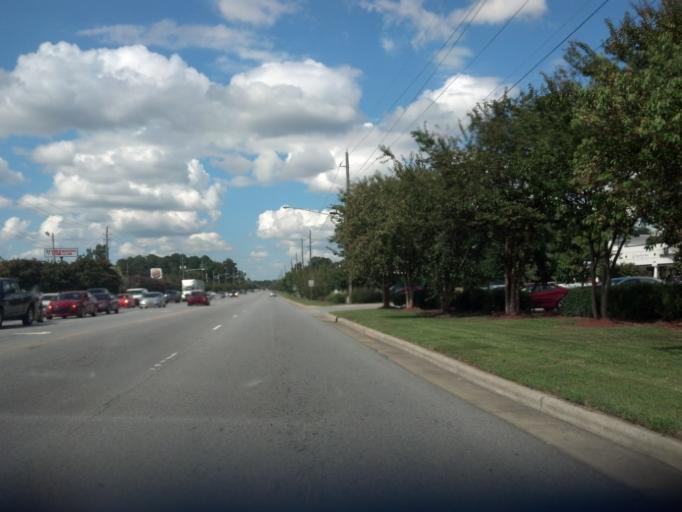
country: US
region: North Carolina
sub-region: Pitt County
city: Windsor
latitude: 35.5672
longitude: -77.3507
